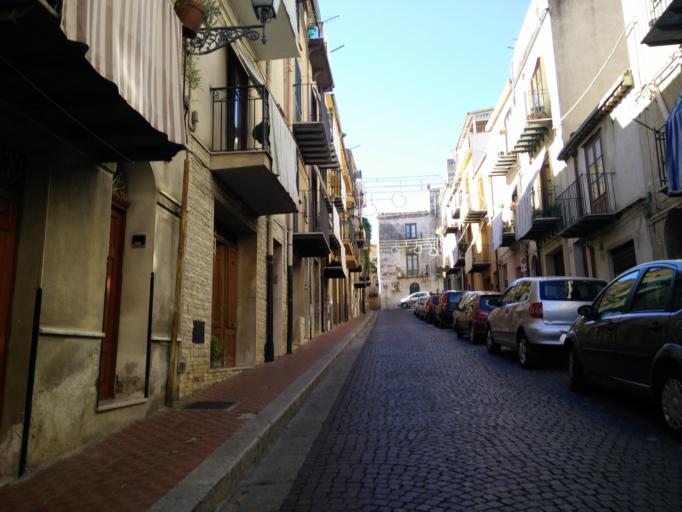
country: IT
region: Sicily
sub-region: Palermo
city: Castelbuono
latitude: 37.9279
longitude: 14.0899
